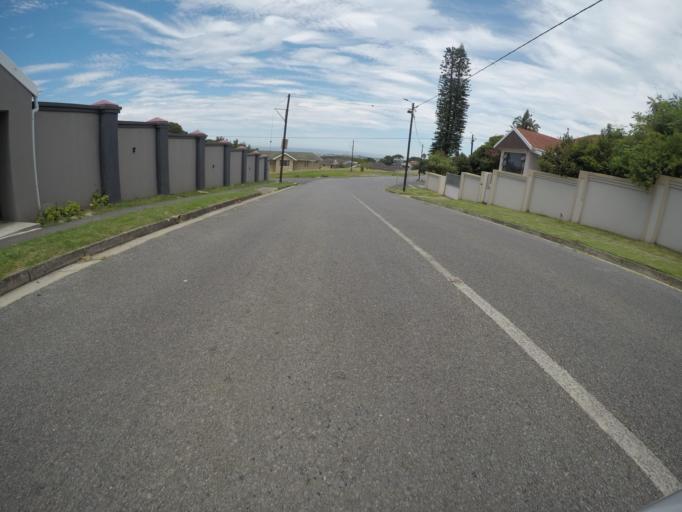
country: ZA
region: Eastern Cape
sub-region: Buffalo City Metropolitan Municipality
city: East London
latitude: -33.0385
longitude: 27.8548
